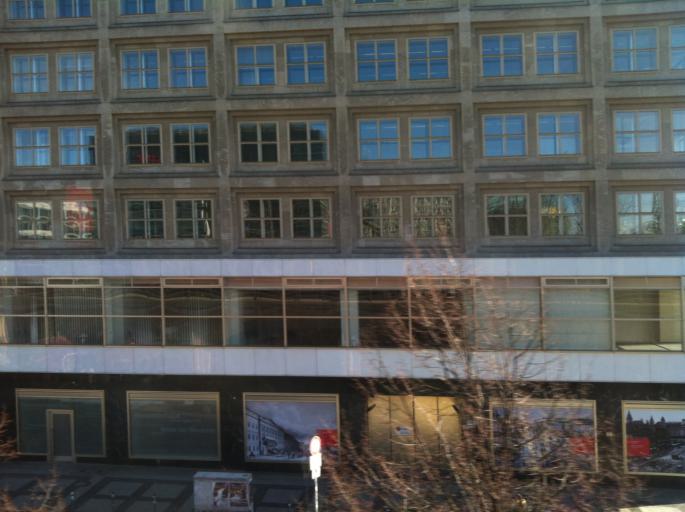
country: DE
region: Berlin
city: Berlin
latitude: 52.5202
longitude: 13.4133
